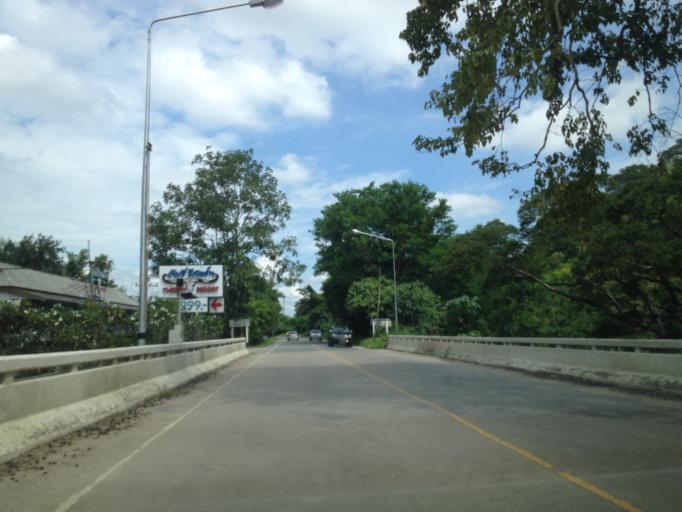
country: TH
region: Chiang Mai
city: Hang Dong
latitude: 18.7377
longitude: 98.8988
